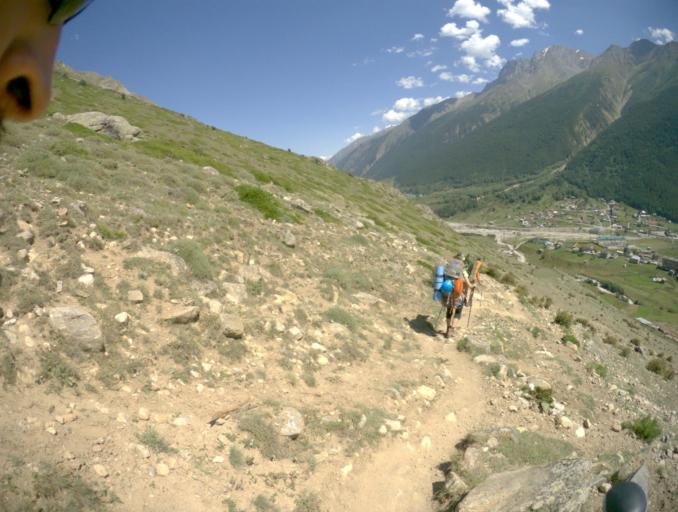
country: RU
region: Kabardino-Balkariya
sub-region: El'brusskiy Rayon
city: El'brus
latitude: 43.2627
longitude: 42.6420
